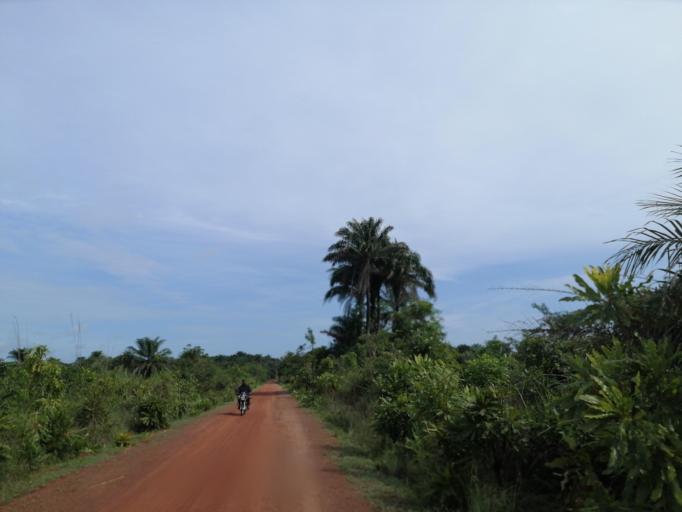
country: SL
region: Northern Province
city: Port Loko
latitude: 8.7738
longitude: -12.9158
